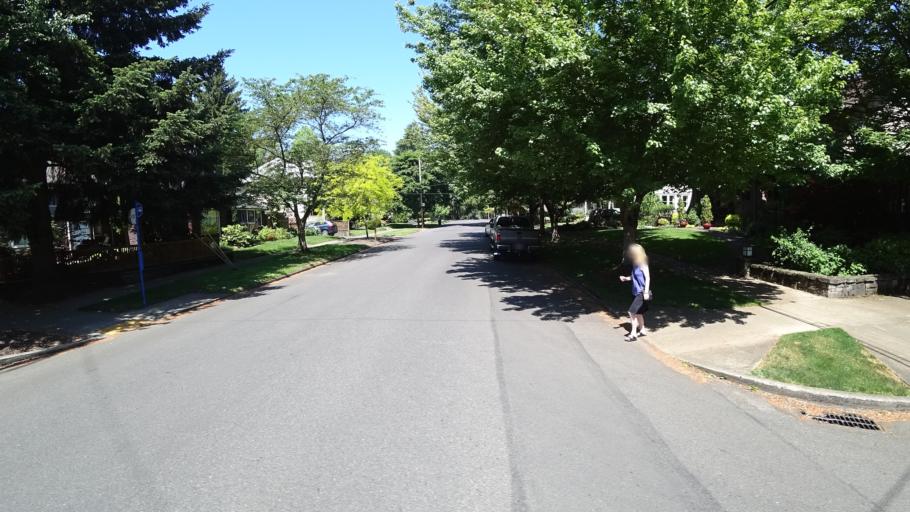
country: US
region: Oregon
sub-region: Multnomah County
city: Portland
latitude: 45.5364
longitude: -122.6412
